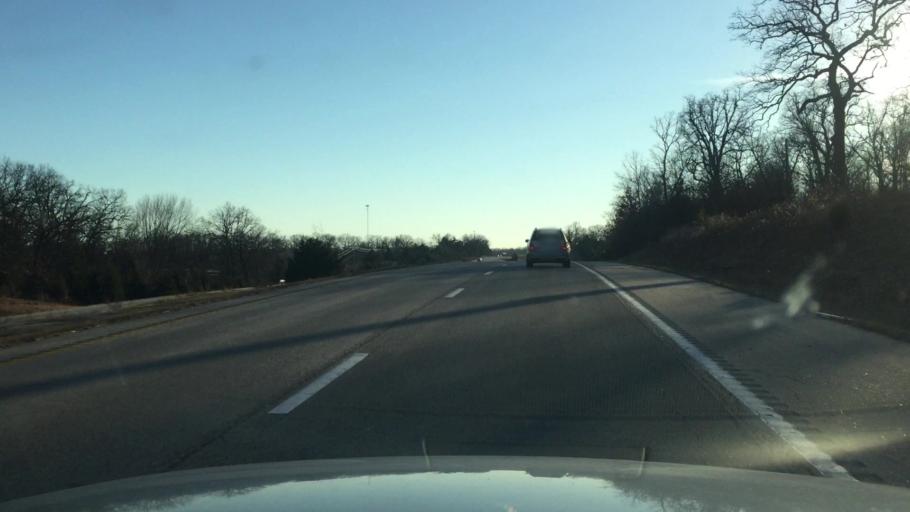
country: US
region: Missouri
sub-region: Cole County
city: Wardsville
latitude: 38.4597
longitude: -92.2968
